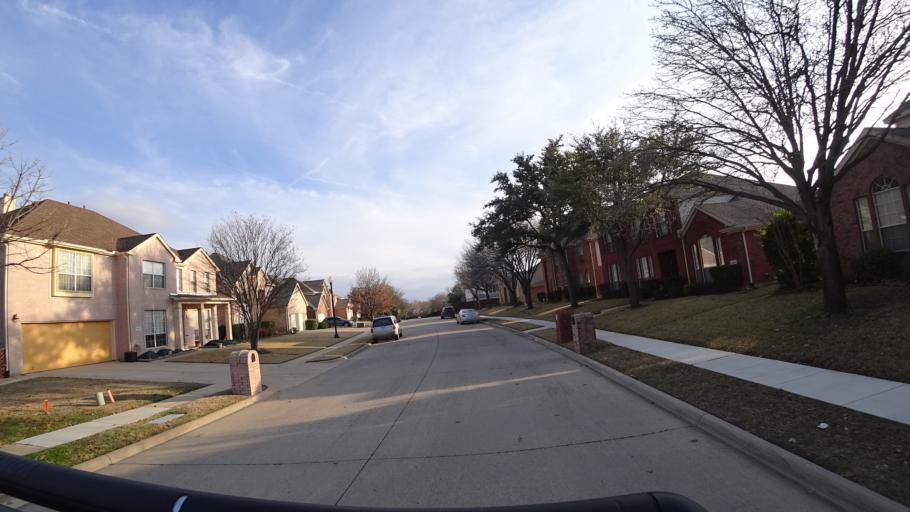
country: US
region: Texas
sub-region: Dallas County
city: Coppell
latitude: 32.9921
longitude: -96.9871
